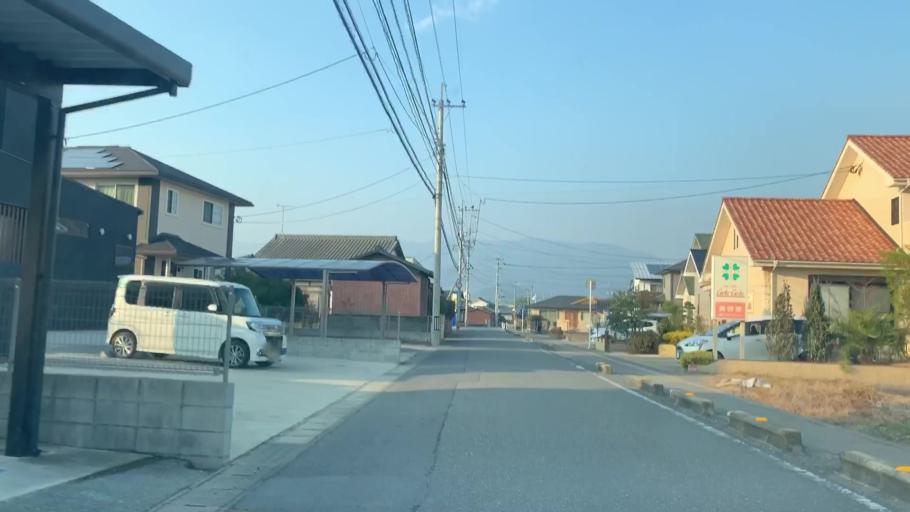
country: JP
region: Saga Prefecture
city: Saga-shi
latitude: 33.2761
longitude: 130.2270
